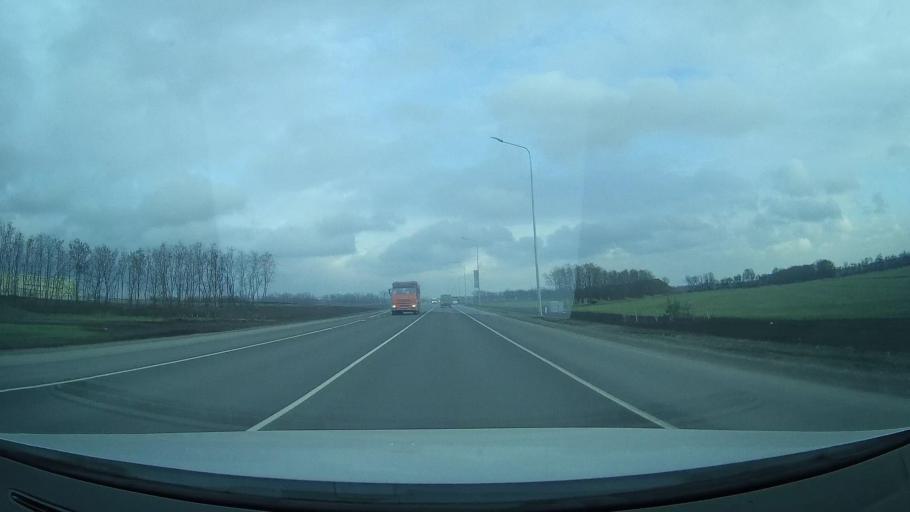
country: RU
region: Rostov
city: Grushevskaya
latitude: 47.4726
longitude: 39.9076
